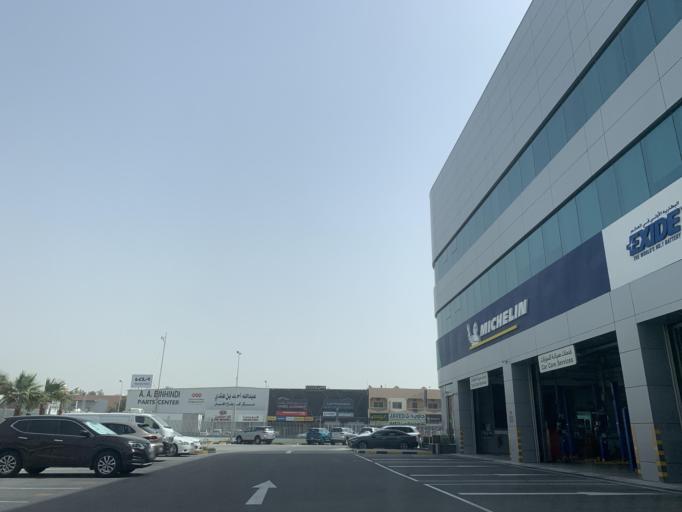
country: BH
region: Northern
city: Madinat `Isa
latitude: 26.1876
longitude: 50.5324
